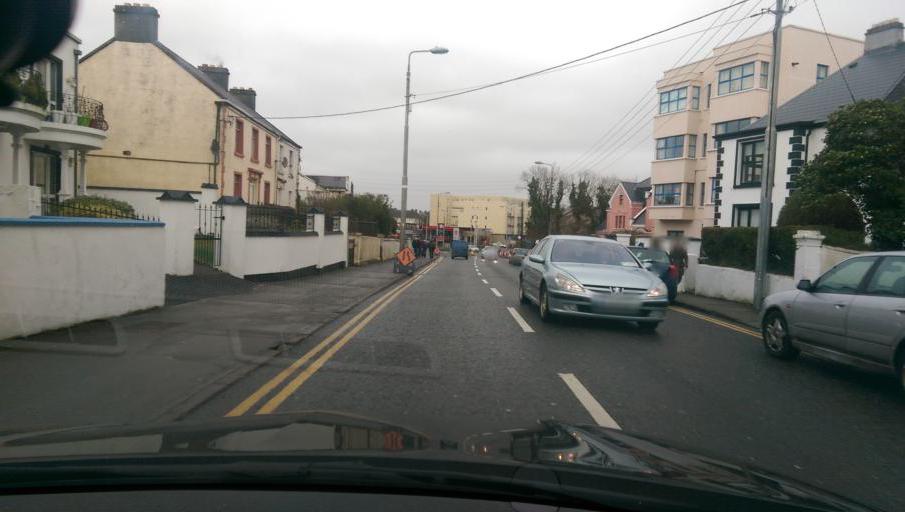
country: IE
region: Connaught
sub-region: County Galway
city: Gaillimh
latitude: 53.2621
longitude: -9.0739
